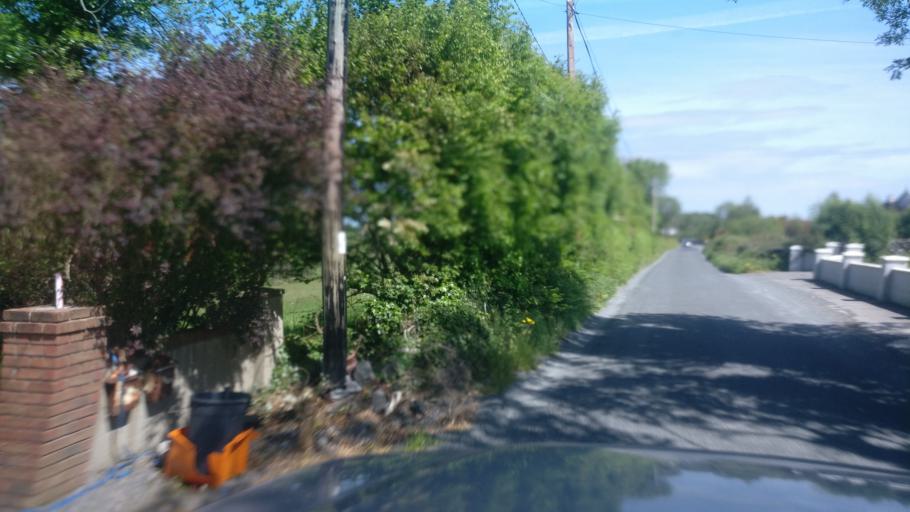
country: IE
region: Connaught
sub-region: County Galway
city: Gort
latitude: 53.0813
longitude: -8.8025
